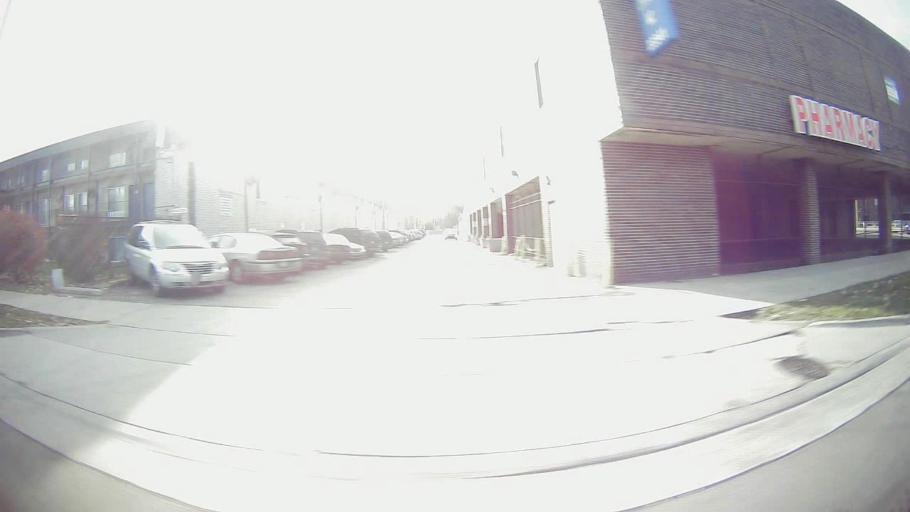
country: US
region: Michigan
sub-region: Oakland County
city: Southfield
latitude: 42.4431
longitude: -83.2630
